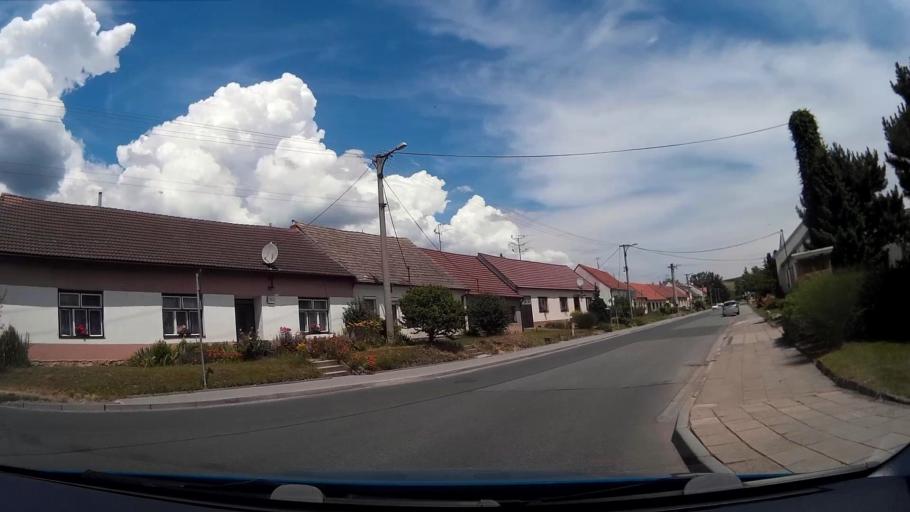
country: CZ
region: South Moravian
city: Dolni Kounice
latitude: 49.0537
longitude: 16.4792
